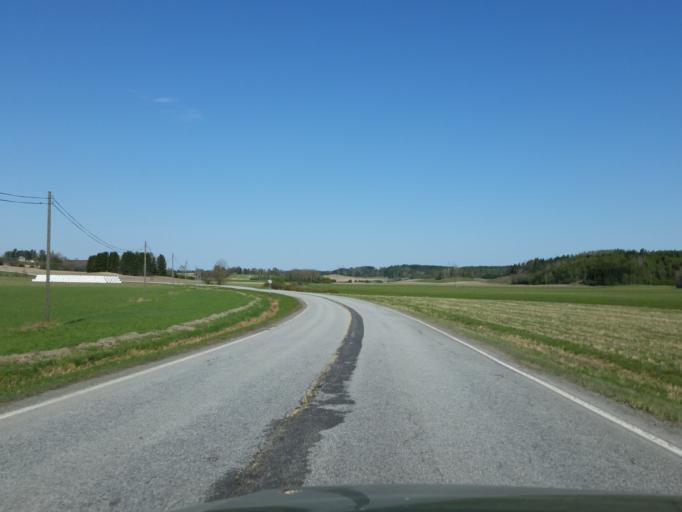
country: FI
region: Uusimaa
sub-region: Helsinki
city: Siuntio
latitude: 60.1734
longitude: 24.1614
